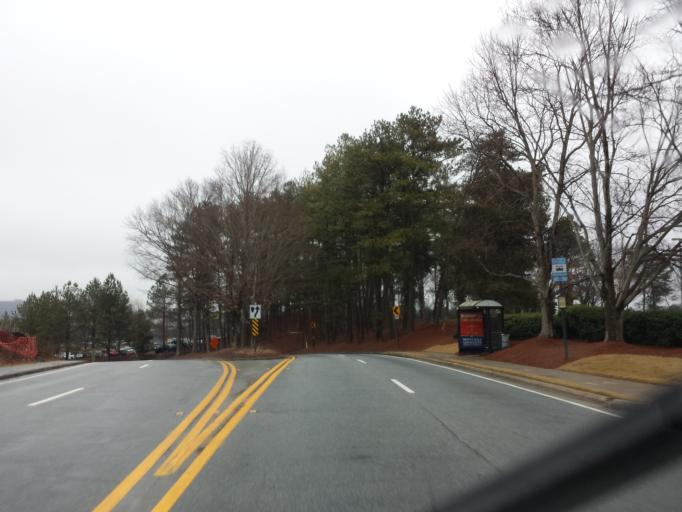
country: US
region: Georgia
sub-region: Cobb County
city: Vinings
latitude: 33.8905
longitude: -84.4653
